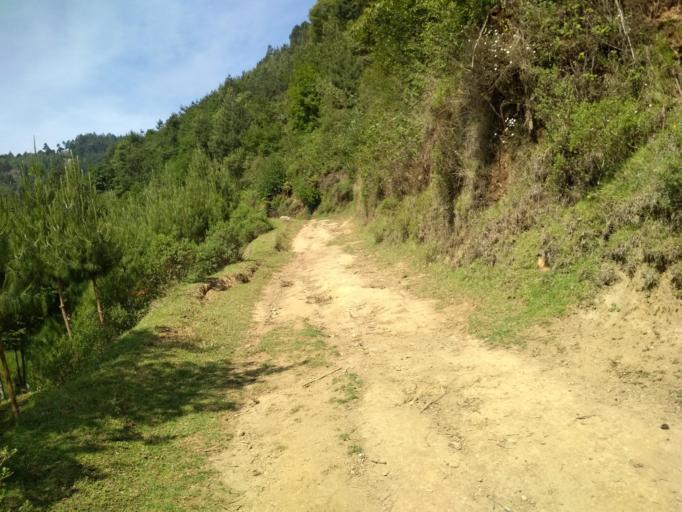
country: MX
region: Veracruz
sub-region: Mariano Escobedo
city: San Isidro el Berro
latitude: 18.9413
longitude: -97.2201
